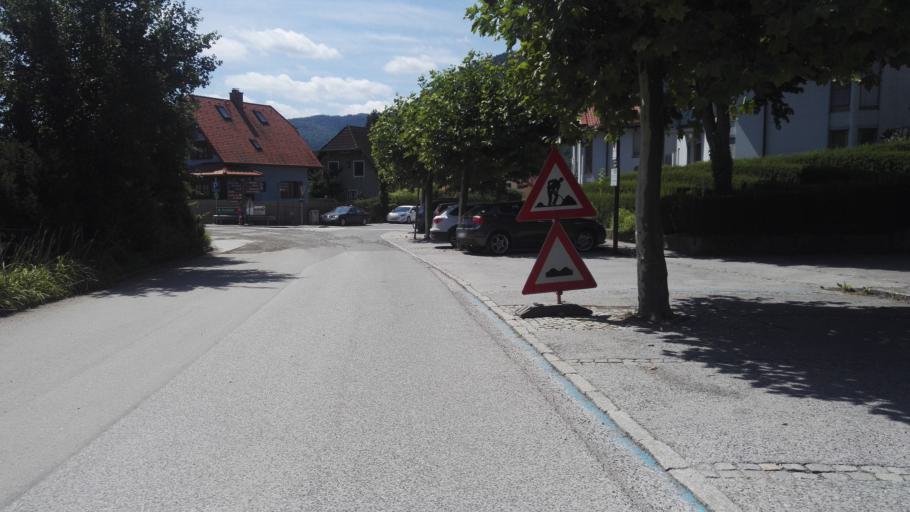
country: AT
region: Styria
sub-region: Politischer Bezirk Graz-Umgebung
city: Frohnleiten
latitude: 47.2690
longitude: 15.3216
